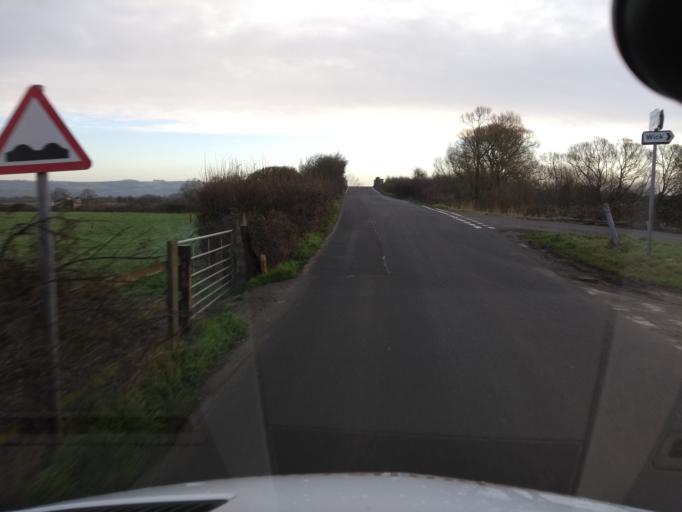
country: GB
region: England
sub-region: North Somerset
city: Bleadon
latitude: 51.2843
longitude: -2.9718
